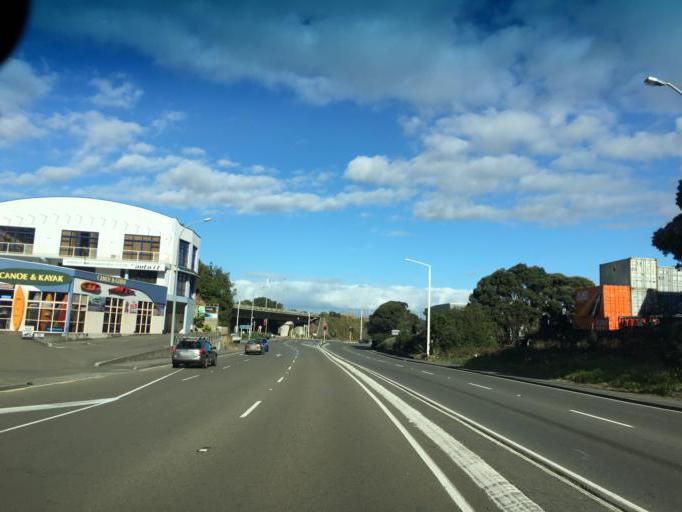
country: NZ
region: Wellington
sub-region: Wellington City
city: Wellington
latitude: -41.2459
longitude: 174.8135
